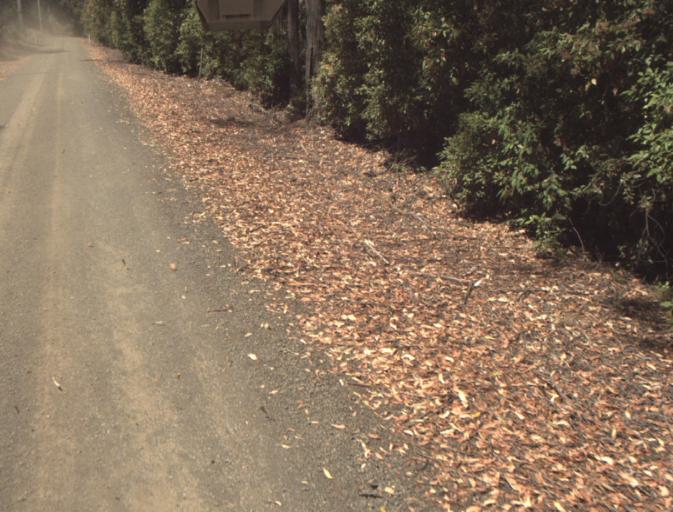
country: AU
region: Tasmania
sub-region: Dorset
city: Scottsdale
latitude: -41.3549
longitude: 147.3907
